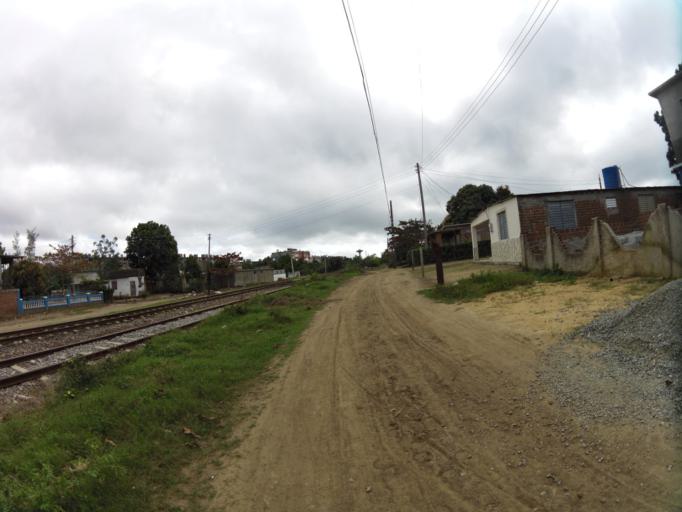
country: CU
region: Las Tunas
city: Las Tunas
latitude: 20.9632
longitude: -76.9354
